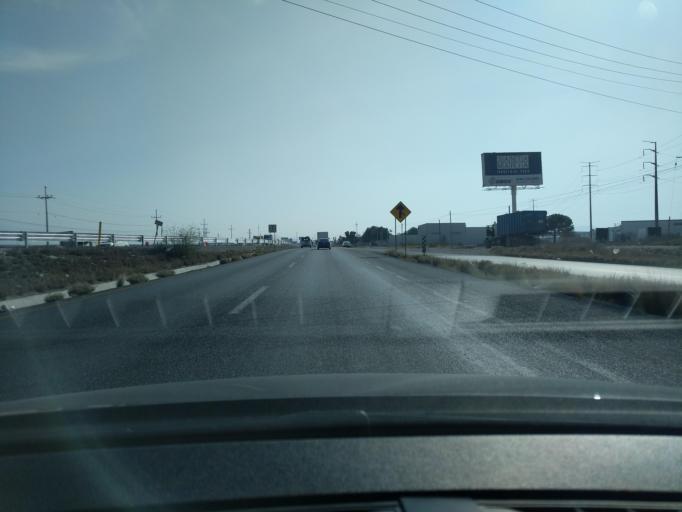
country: MX
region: Coahuila
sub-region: Ramos Arizpe
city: Ramos Arizpe
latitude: 25.6086
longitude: -100.8612
